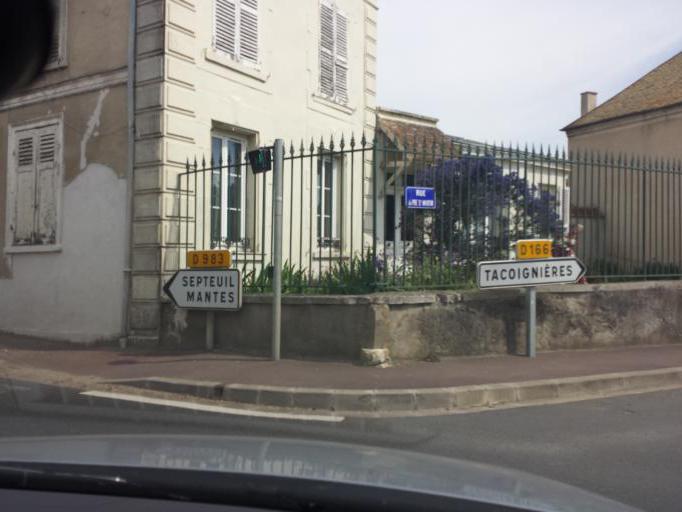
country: FR
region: Ile-de-France
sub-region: Departement des Yvelines
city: Tacoignieres
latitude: 48.8601
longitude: 1.6415
